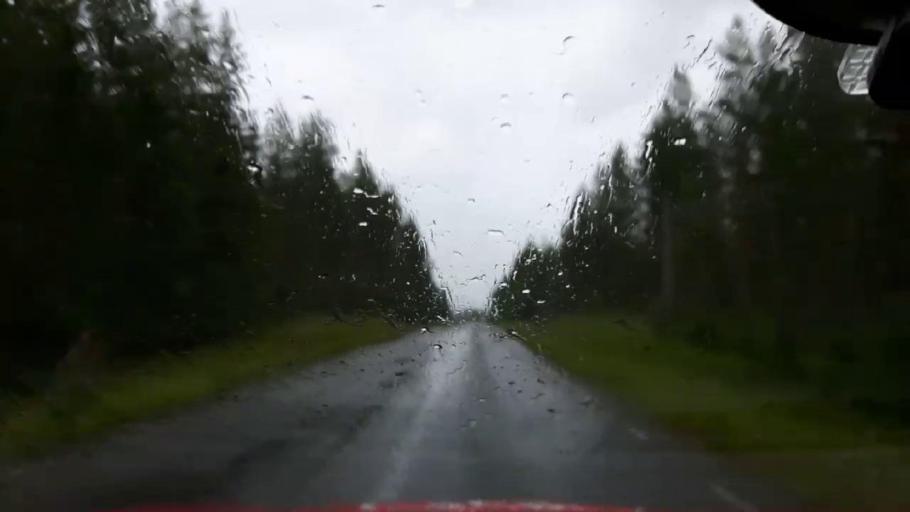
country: SE
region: Jaemtland
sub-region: OEstersunds Kommun
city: Brunflo
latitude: 62.9987
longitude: 14.7602
